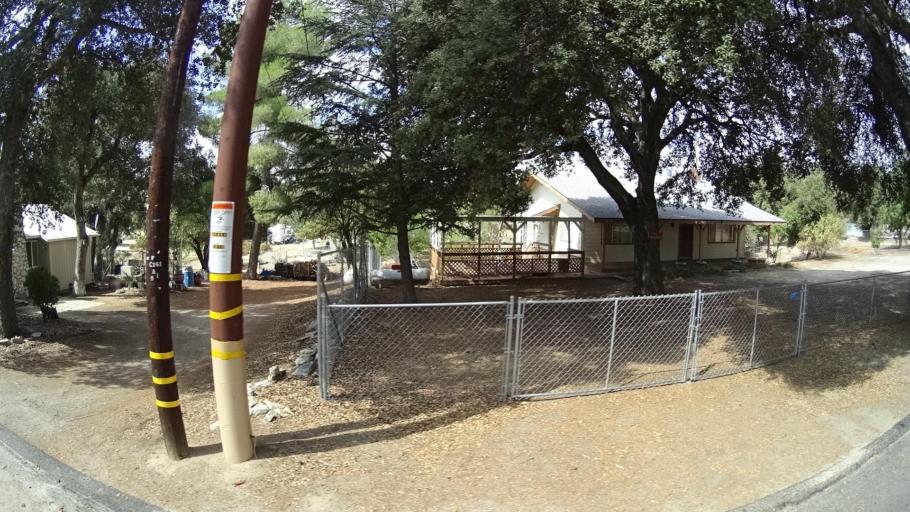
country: US
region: California
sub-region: San Diego County
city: Campo
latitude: 32.6916
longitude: -116.3342
